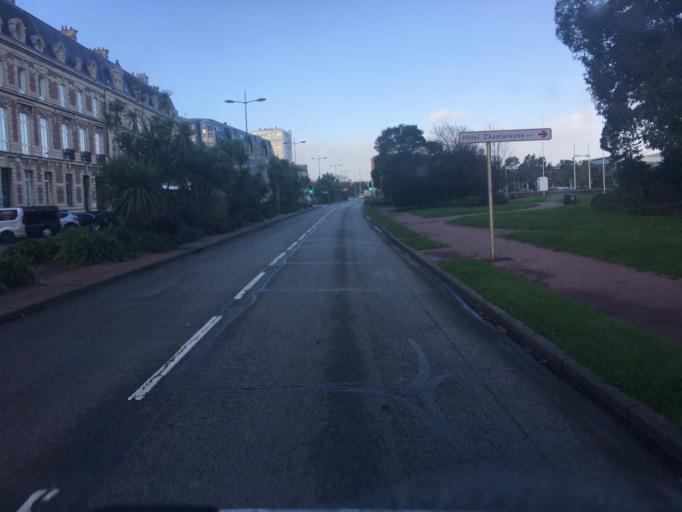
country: FR
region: Lower Normandy
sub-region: Departement de la Manche
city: Cherbourg-Octeville
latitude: 49.6433
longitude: -1.6248
